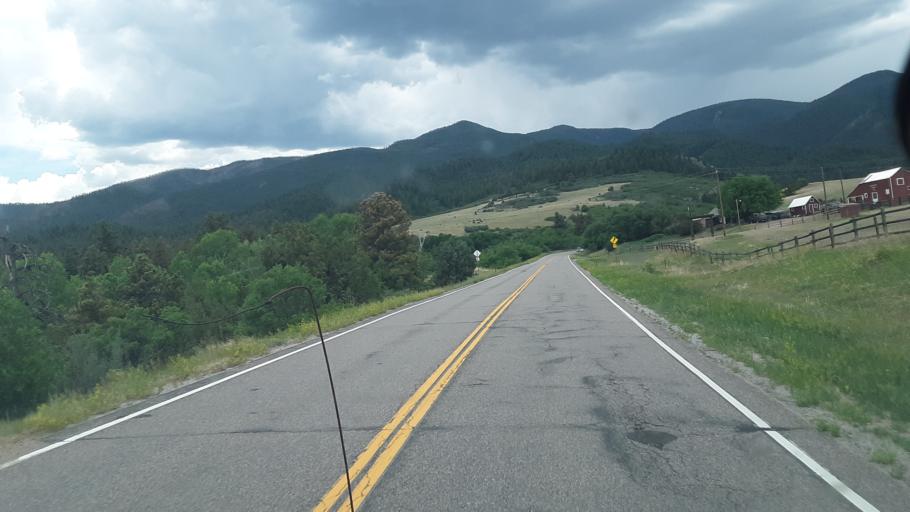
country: US
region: Colorado
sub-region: Fremont County
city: Florence
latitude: 38.1849
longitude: -105.1049
